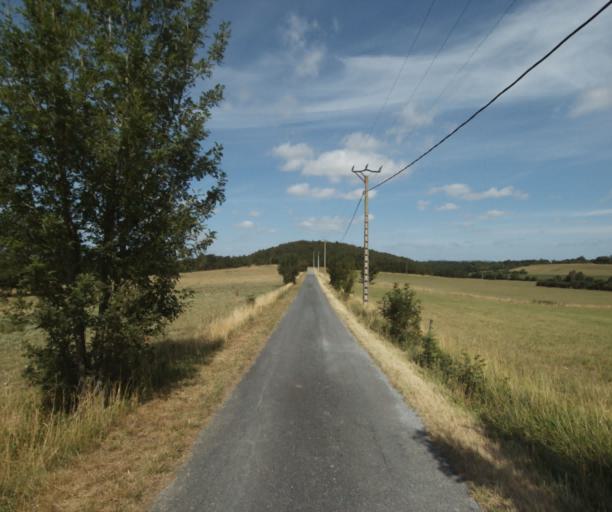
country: FR
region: Midi-Pyrenees
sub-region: Departement du Tarn
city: Dourgne
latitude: 43.4738
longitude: 2.1148
